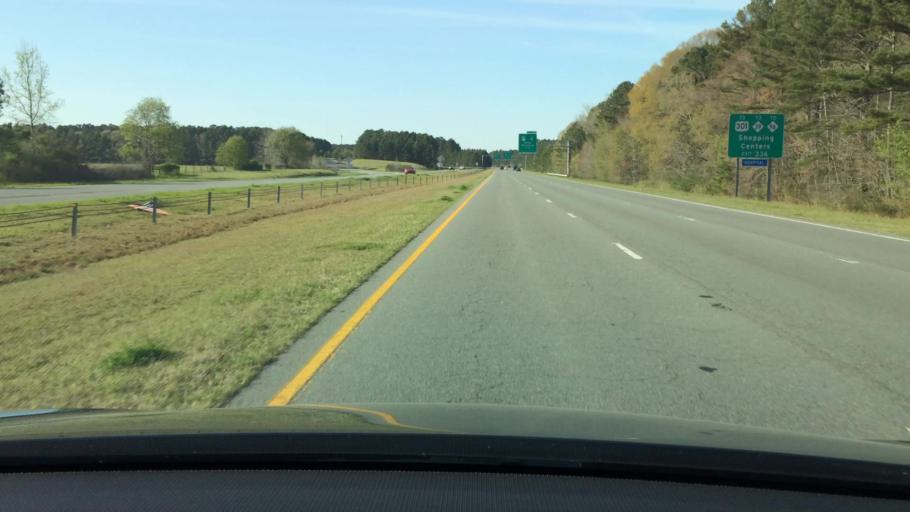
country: US
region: North Carolina
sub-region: Johnston County
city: Selma
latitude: 35.5035
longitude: -78.2808
